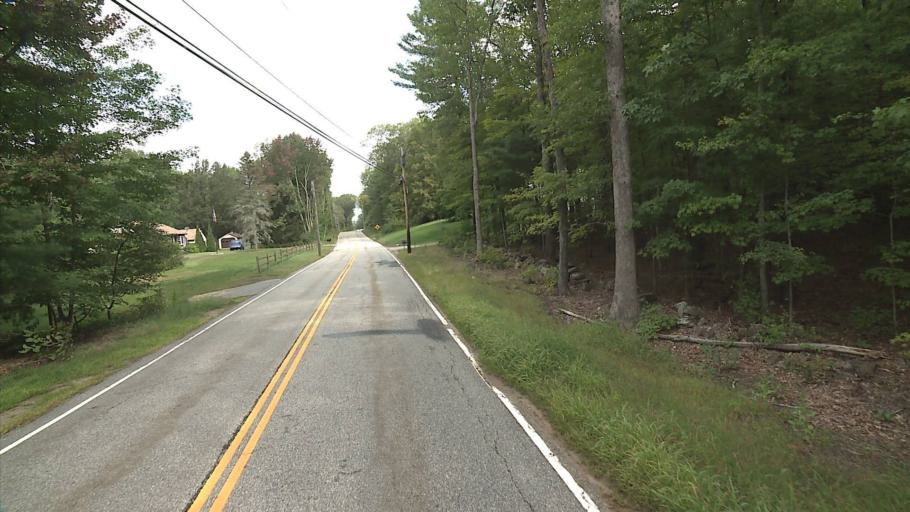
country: US
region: Connecticut
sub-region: Tolland County
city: Stafford Springs
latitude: 41.8882
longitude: -72.2677
